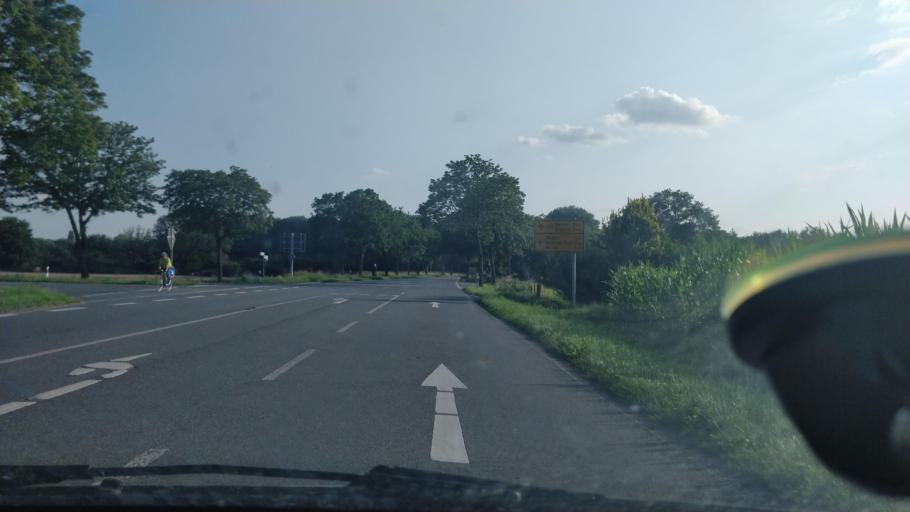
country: DE
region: North Rhine-Westphalia
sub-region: Regierungsbezirk Dusseldorf
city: Rheurdt
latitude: 51.4799
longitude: 6.4878
